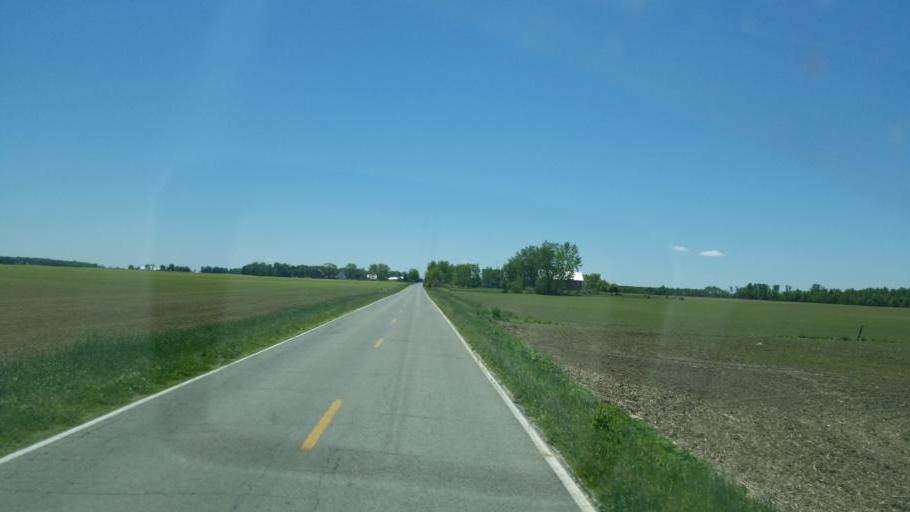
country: US
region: Indiana
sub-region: Randolph County
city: Union City
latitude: 40.2899
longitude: -84.8039
